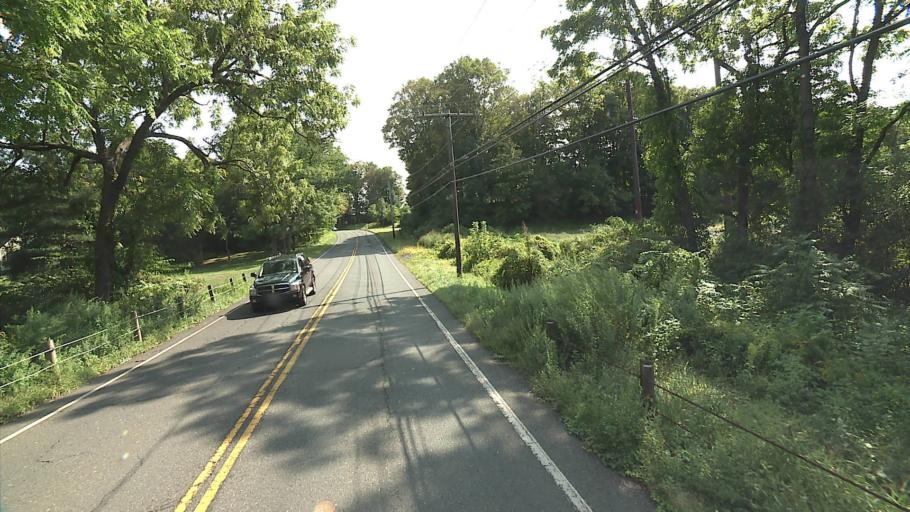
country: US
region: Connecticut
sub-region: New Haven County
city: Heritage Village
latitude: 41.4815
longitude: -73.2572
